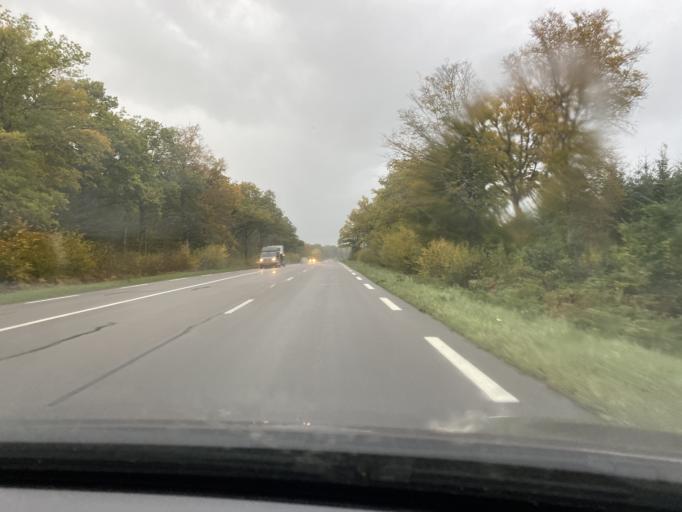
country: FR
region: Bourgogne
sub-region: Departement de la Cote-d'Or
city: Saulieu
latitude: 47.3270
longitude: 4.1934
